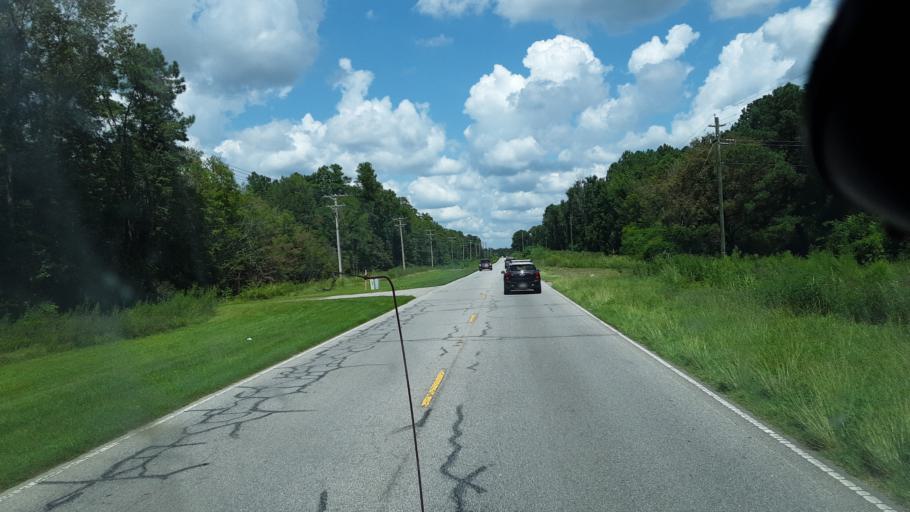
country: US
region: South Carolina
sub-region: Williamsburg County
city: Andrews
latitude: 33.4782
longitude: -79.5566
